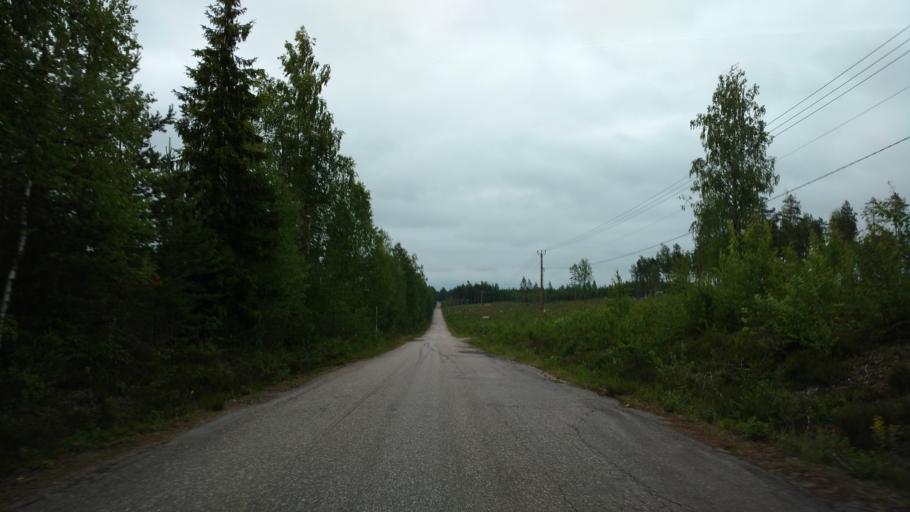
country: FI
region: Varsinais-Suomi
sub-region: Salo
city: Kiikala
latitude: 60.4649
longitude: 23.6435
